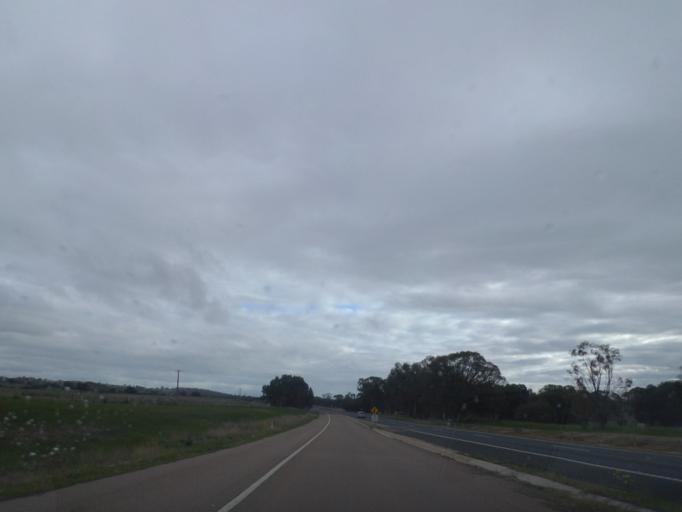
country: AU
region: Victoria
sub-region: Wangaratta
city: Wangaratta
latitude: -36.2230
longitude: 146.4451
